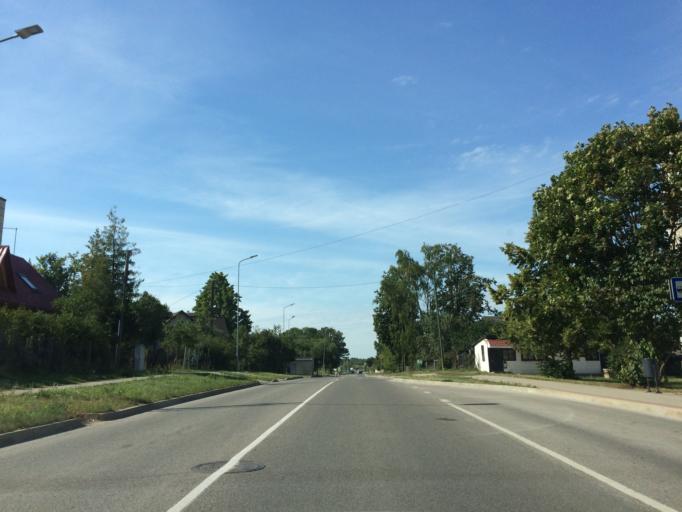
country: LV
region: Rezekne
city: Rezekne
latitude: 56.5158
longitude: 27.3304
